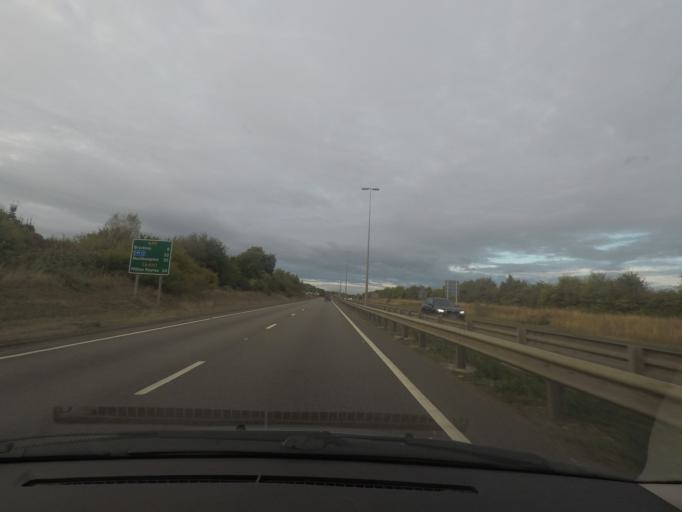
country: GB
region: England
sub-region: Oxfordshire
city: Somerton
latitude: 51.9536
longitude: -1.2041
